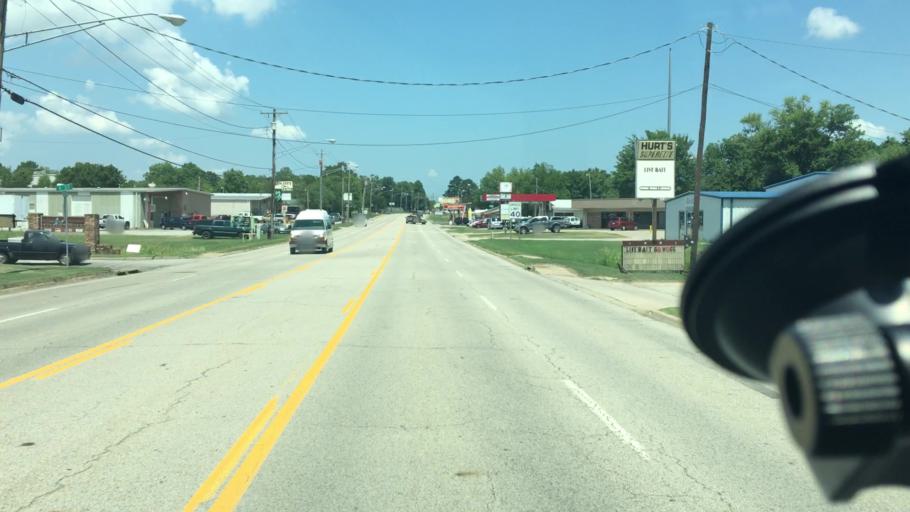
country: US
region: Arkansas
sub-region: Sebastian County
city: Barling
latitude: 35.3266
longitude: -94.3032
